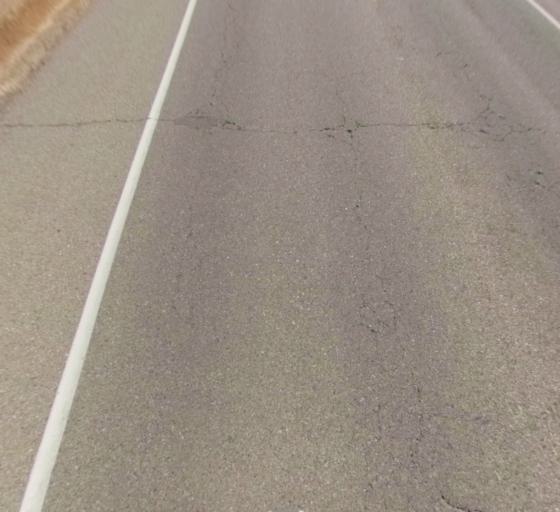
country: US
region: California
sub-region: Fresno County
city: Biola
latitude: 36.8501
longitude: -120.0746
